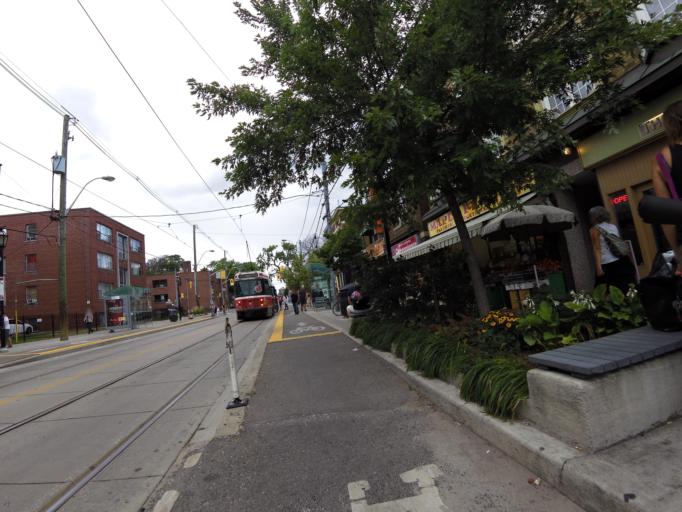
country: CA
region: Ontario
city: Toronto
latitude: 43.6458
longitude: -79.4488
